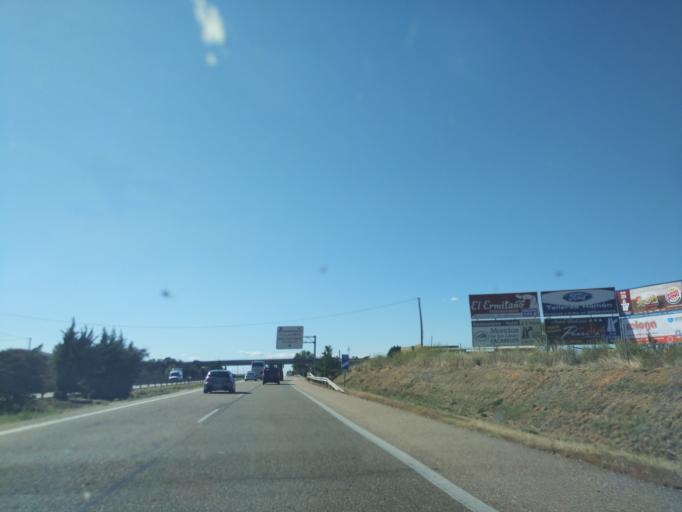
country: ES
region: Castille and Leon
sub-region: Provincia de Zamora
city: San Esteban del Molar
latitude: 41.9399
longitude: -5.5496
